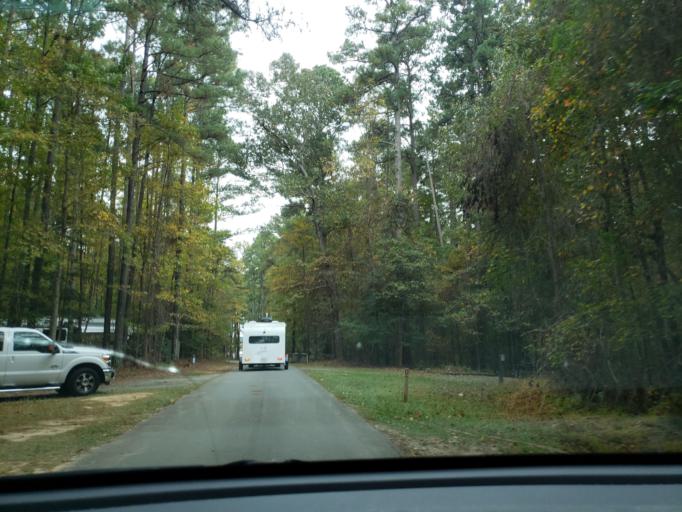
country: US
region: North Carolina
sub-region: Chatham County
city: Fearrington Village
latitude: 35.7422
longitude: -79.0358
